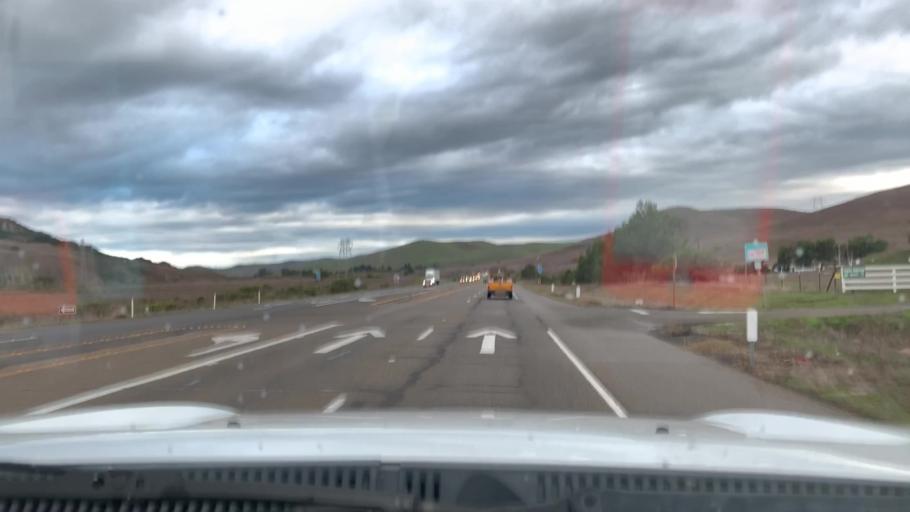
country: US
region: California
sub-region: San Luis Obispo County
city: Los Osos
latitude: 35.3448
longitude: -120.7666
